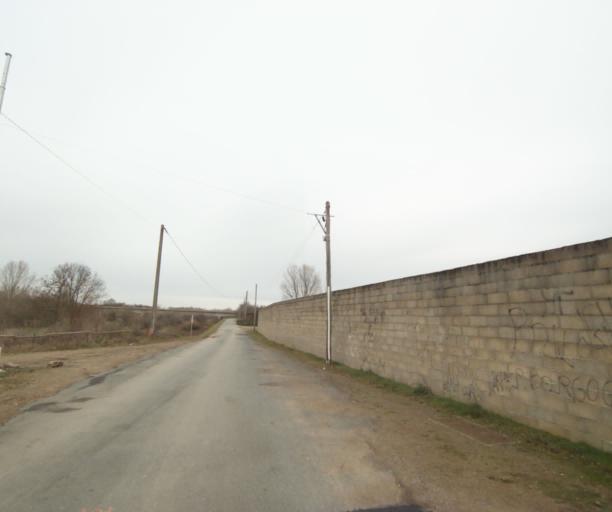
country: FR
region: Rhone-Alpes
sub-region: Departement de la Loire
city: Le Coteau
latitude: 46.0411
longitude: 4.0899
